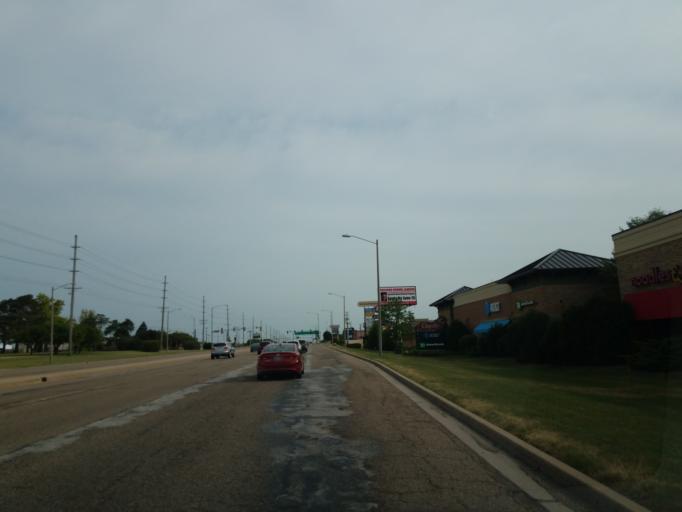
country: US
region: Illinois
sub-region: McLean County
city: Bloomington
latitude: 40.4820
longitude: -88.9525
